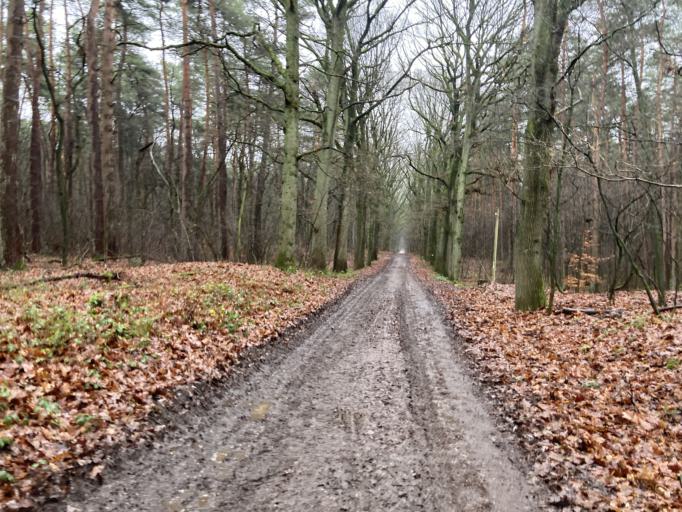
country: DE
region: North Rhine-Westphalia
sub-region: Regierungsbezirk Dusseldorf
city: Niederkruchten
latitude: 51.1745
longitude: 6.1995
